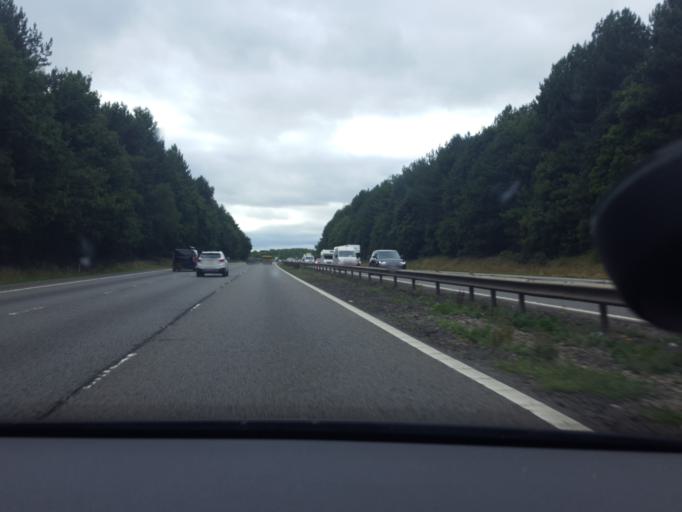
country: GB
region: England
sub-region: Leicestershire
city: Markfield
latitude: 52.6581
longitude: -1.2531
